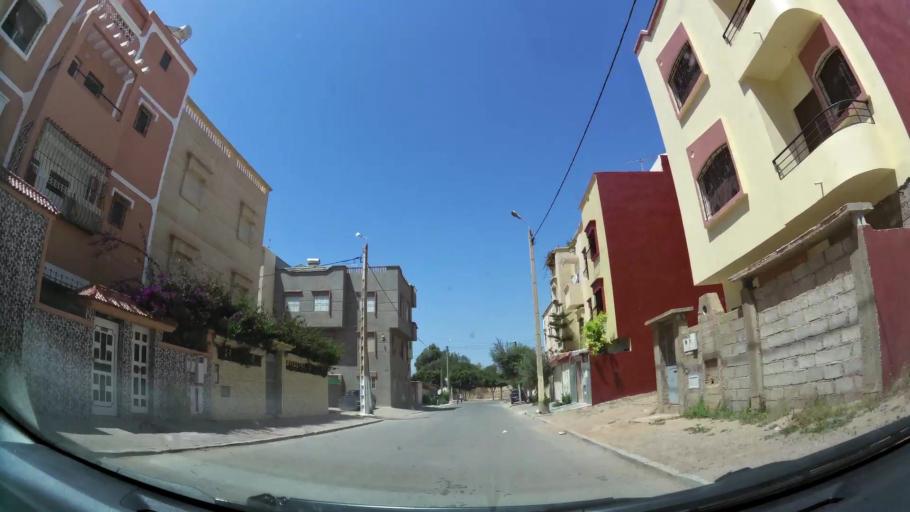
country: MA
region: Souss-Massa-Draa
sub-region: Inezgane-Ait Mellou
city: Inezgane
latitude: 30.3509
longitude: -9.4853
